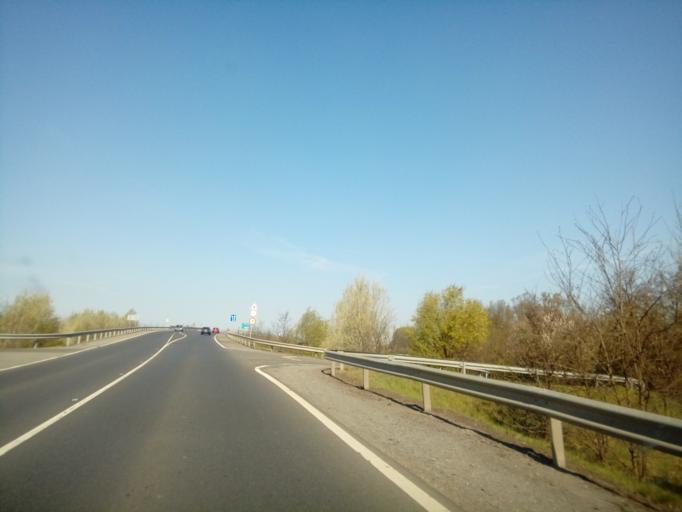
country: HU
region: Szabolcs-Szatmar-Bereg
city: Nagykallo
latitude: 47.8911
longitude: 21.8083
